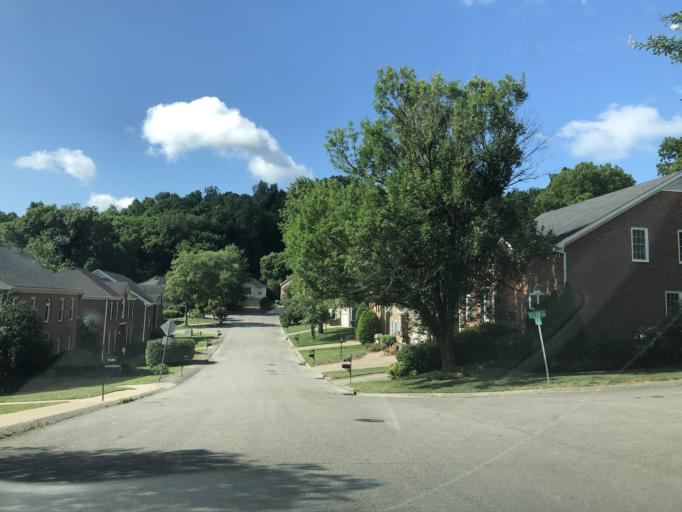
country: US
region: Tennessee
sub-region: Cheatham County
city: Pegram
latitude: 36.0621
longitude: -86.9570
